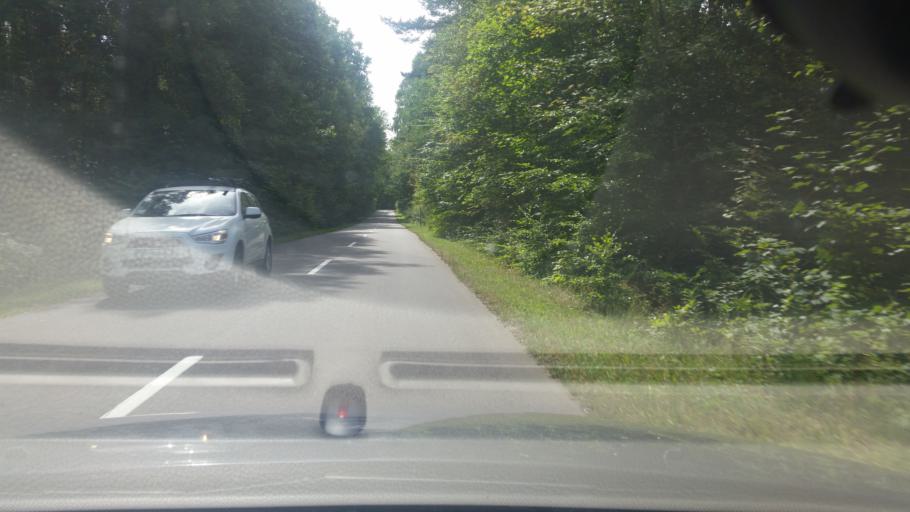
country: PL
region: Pomeranian Voivodeship
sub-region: Powiat wejherowski
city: Choczewo
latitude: 54.7509
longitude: 17.7465
